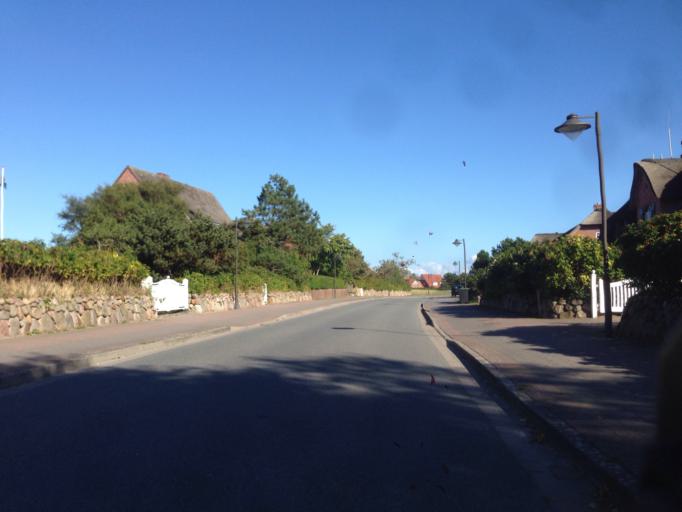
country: DE
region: Schleswig-Holstein
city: List
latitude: 55.0215
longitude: 8.4294
